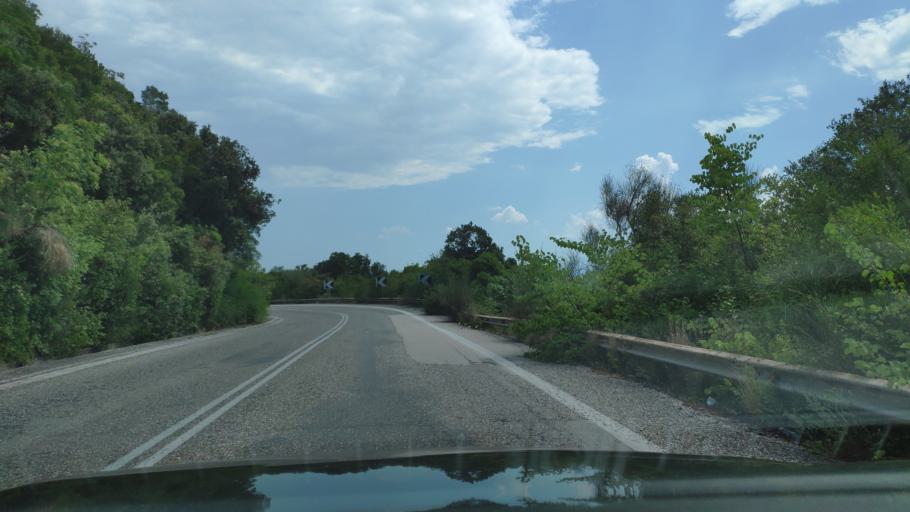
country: GR
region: West Greece
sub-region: Nomos Aitolias kai Akarnanias
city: Menidi
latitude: 39.0037
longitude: 21.1476
